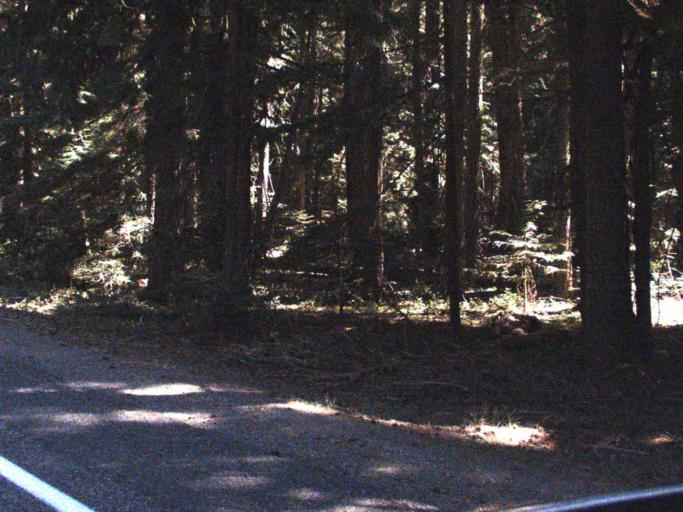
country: US
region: Washington
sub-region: King County
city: Enumclaw
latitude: 46.9838
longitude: -121.5354
